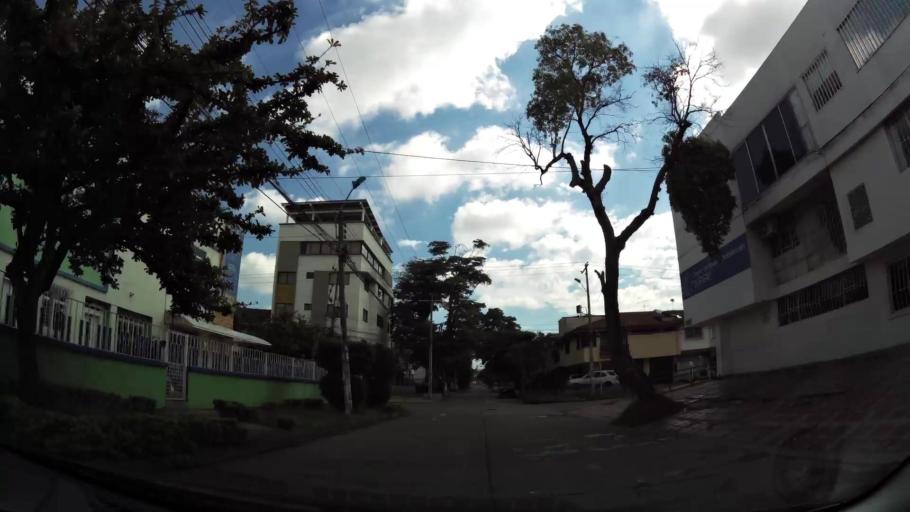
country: CO
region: Valle del Cauca
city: Cali
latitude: 3.4264
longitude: -76.5420
